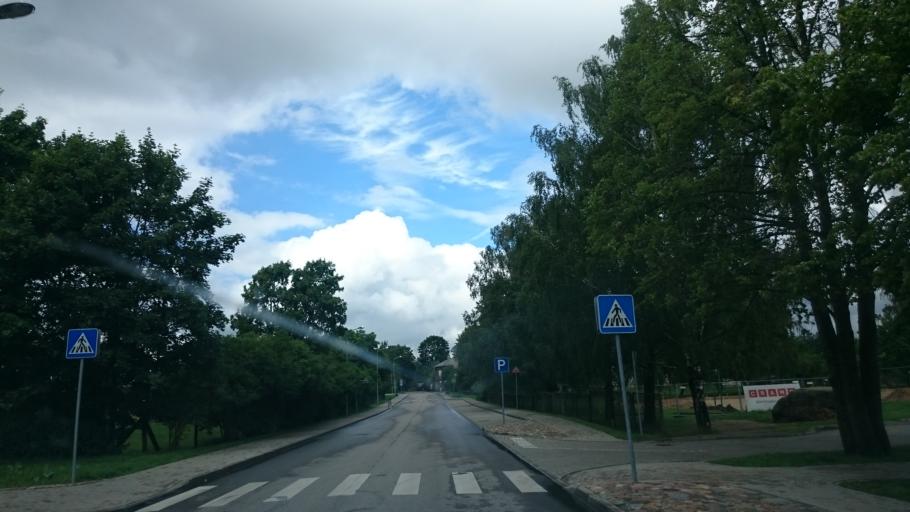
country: LV
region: Aizpute
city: Aizpute
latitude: 56.7203
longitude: 21.6077
